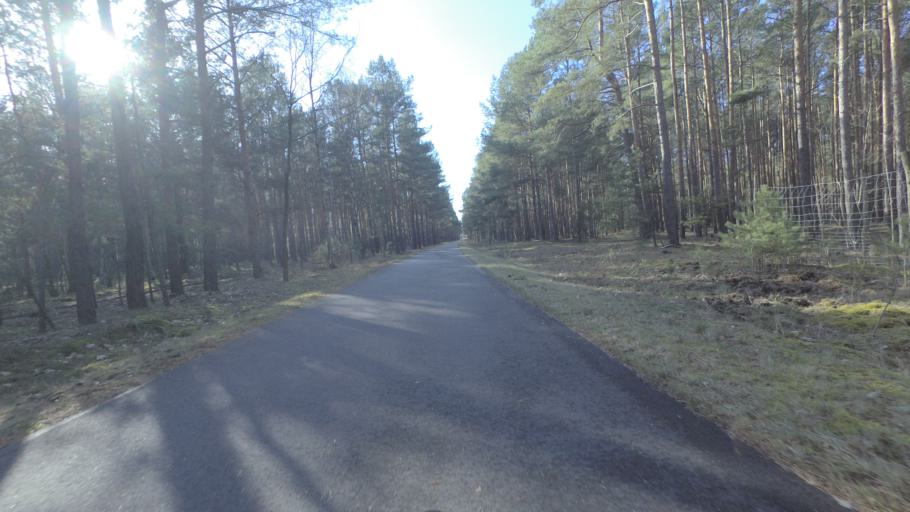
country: DE
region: Brandenburg
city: Luckenwalde
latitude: 52.0521
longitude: 13.1504
